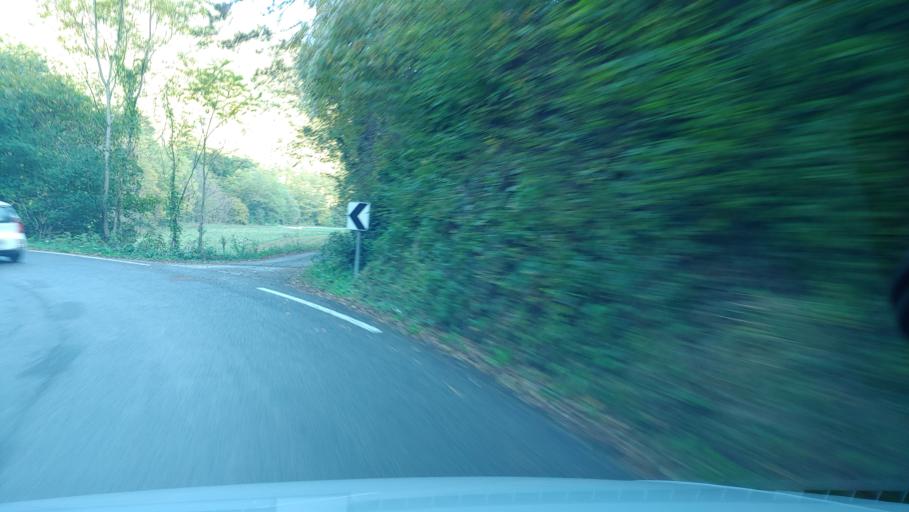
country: SI
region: Ajdovscina
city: Ajdovscina
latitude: 45.8031
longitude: 13.8669
